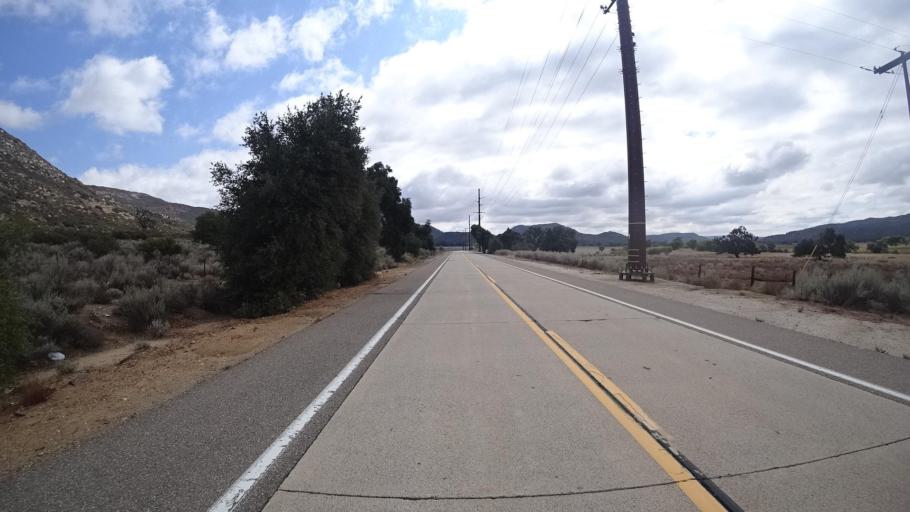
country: US
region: California
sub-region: San Diego County
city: Pine Valley
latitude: 32.7487
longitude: -116.4834
